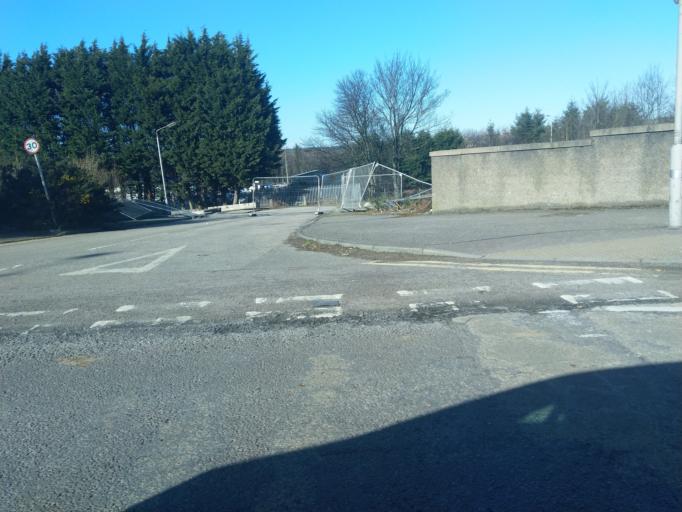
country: GB
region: Scotland
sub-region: Aberdeen City
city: Dyce
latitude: 57.1731
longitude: -2.1459
